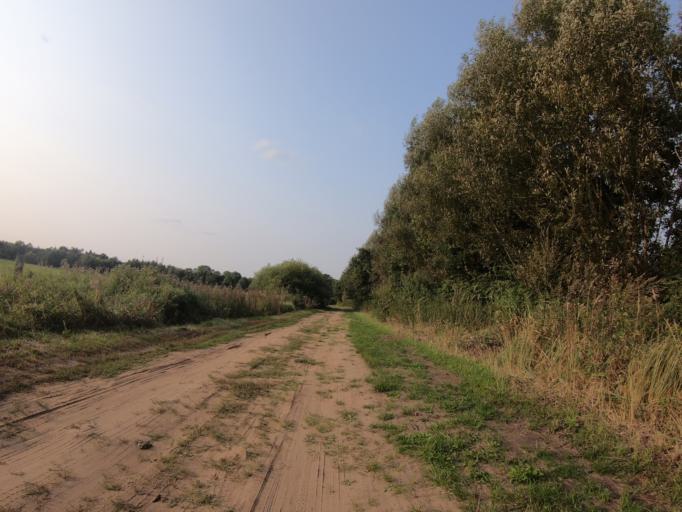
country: DE
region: Lower Saxony
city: Leiferde
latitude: 52.4763
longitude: 10.4659
